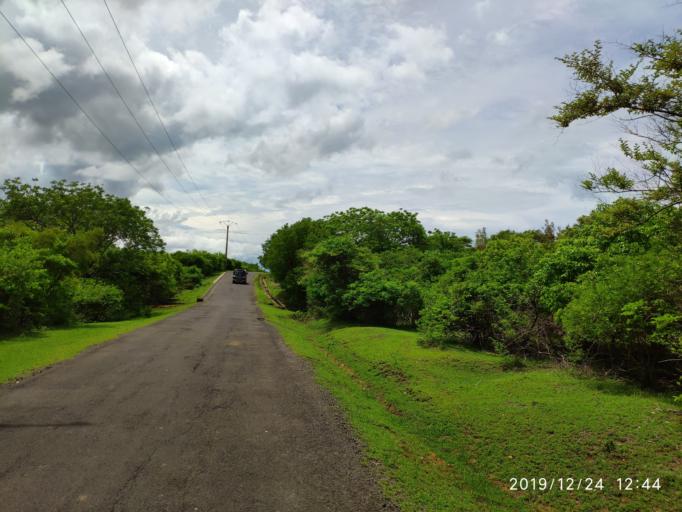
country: MG
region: Diana
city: Antsiranana
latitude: -12.2732
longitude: 49.3514
